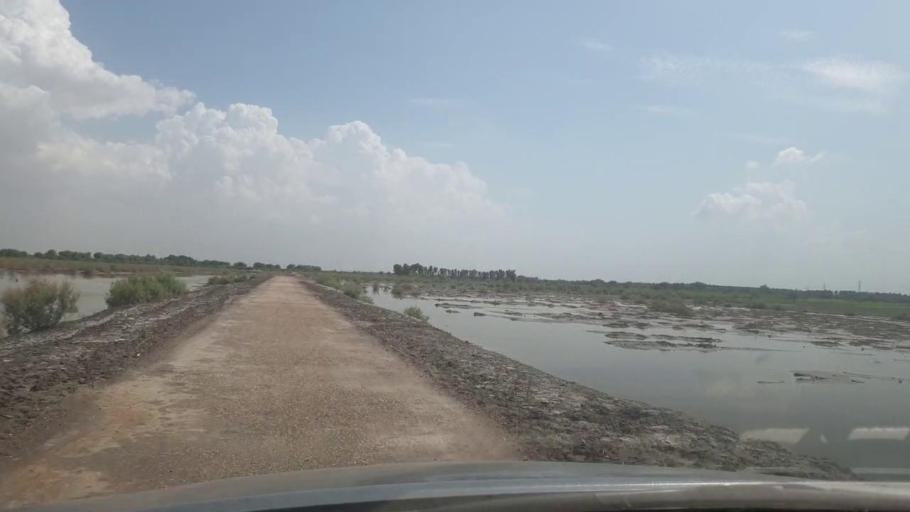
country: PK
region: Sindh
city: Khairpur
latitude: 27.5420
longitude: 68.8038
